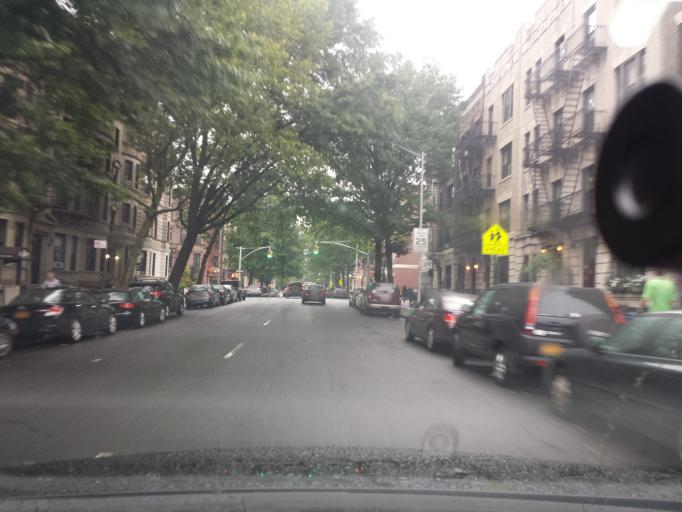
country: US
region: New York
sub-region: Kings County
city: Brooklyn
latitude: 40.6659
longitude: -73.9792
